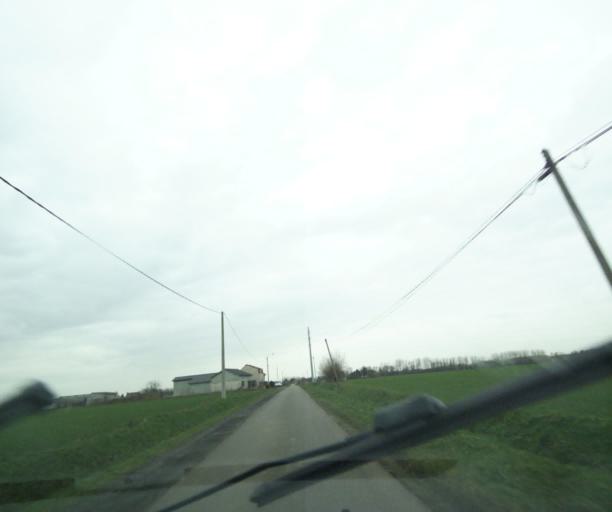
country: FR
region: Nord-Pas-de-Calais
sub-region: Departement du Nord
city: Vicq
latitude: 50.4172
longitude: 3.6159
